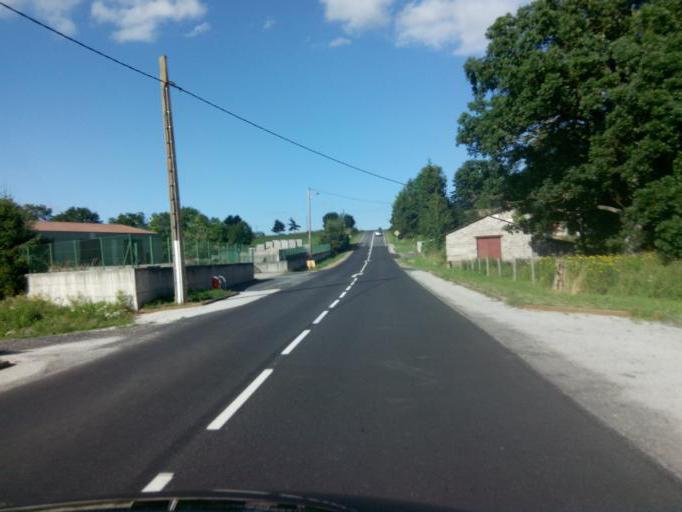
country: FR
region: Auvergne
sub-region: Departement de la Haute-Loire
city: Craponne-sur-Arzon
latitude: 45.3358
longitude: 3.8554
